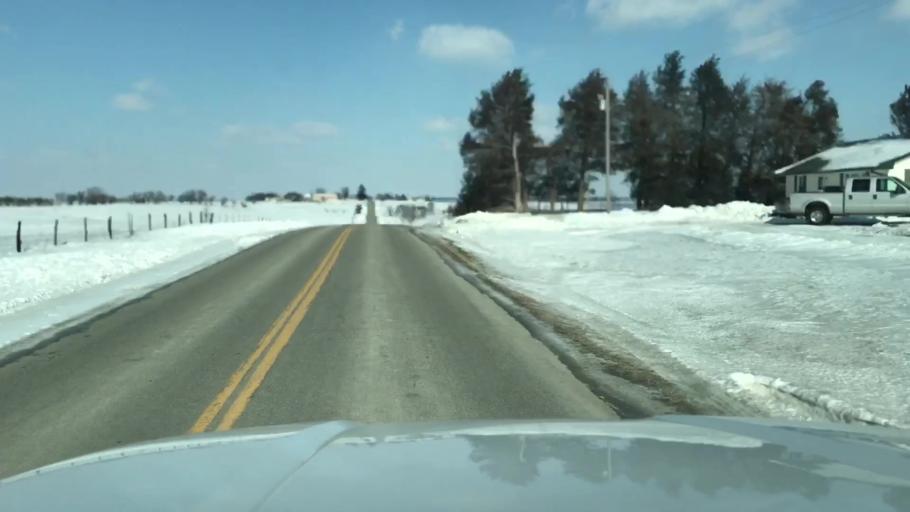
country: US
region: Missouri
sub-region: Nodaway County
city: Maryville
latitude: 40.3732
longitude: -94.7214
